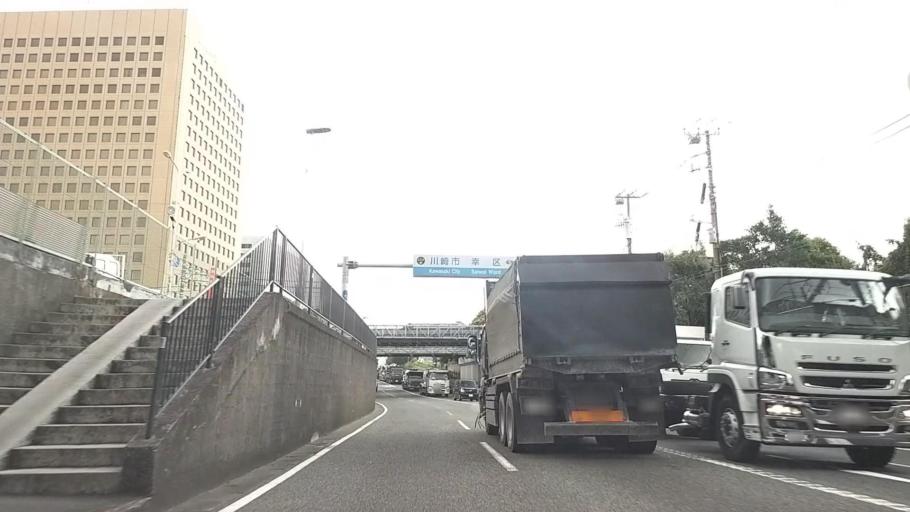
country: JP
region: Kanagawa
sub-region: Kawasaki-shi
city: Kawasaki
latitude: 35.5356
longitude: 139.7034
